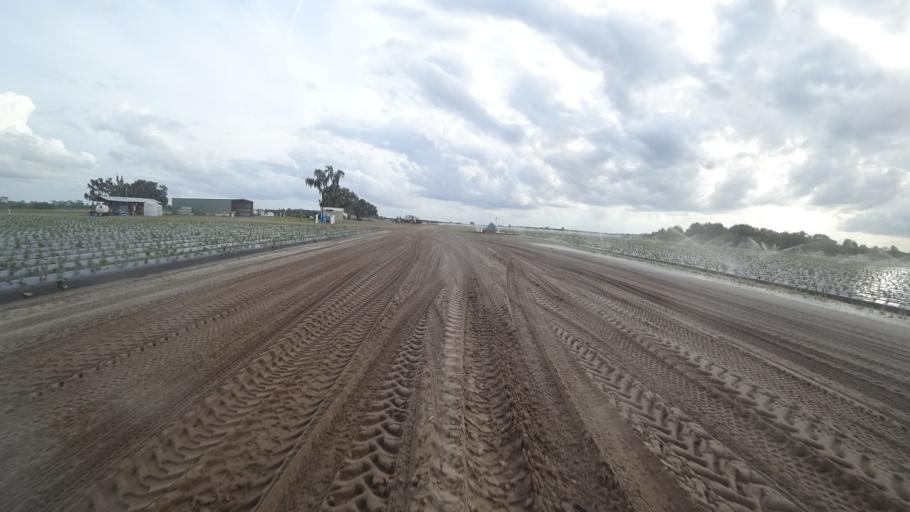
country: US
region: Florida
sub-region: Hillsborough County
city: Wimauma
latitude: 27.5786
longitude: -82.1575
